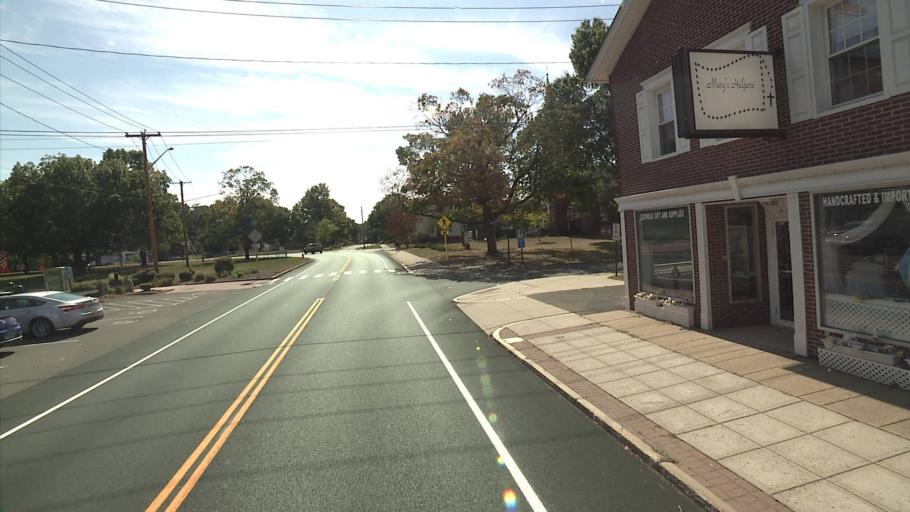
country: US
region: Connecticut
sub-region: New Haven County
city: North Haven
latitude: 41.3872
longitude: -72.8612
